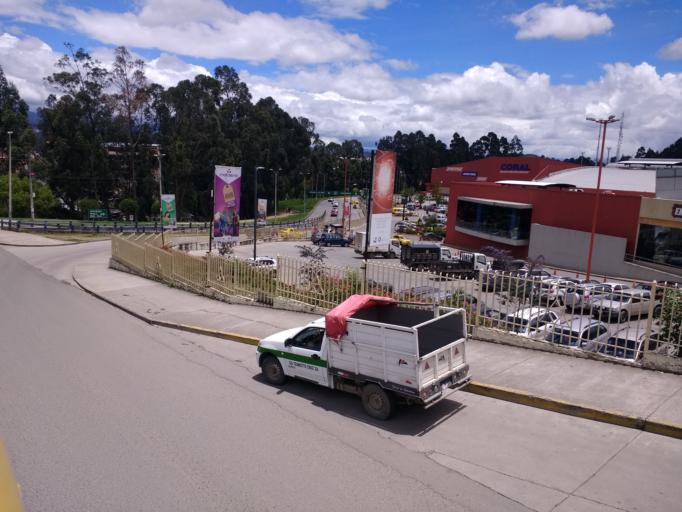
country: EC
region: Azuay
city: Cuenca
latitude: -2.9204
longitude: -79.0155
